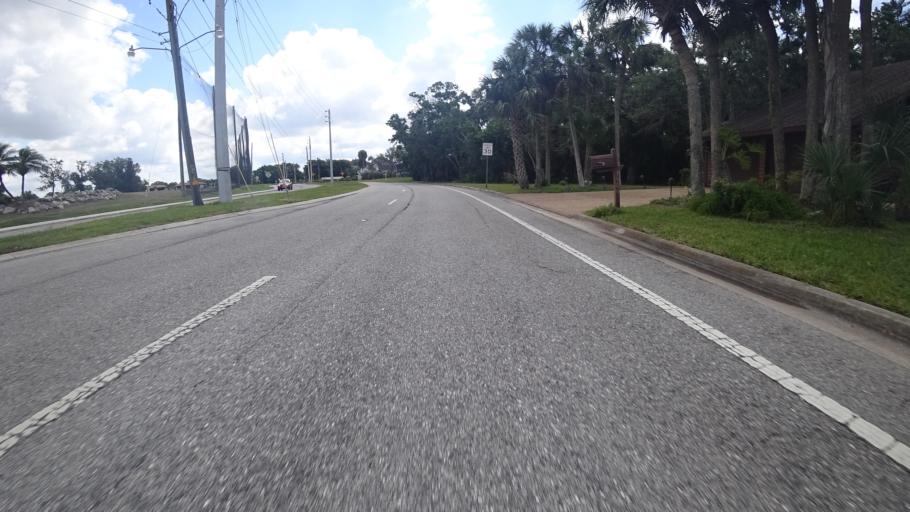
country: US
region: Florida
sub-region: Manatee County
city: Bayshore Gardens
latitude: 27.4290
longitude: -82.6045
